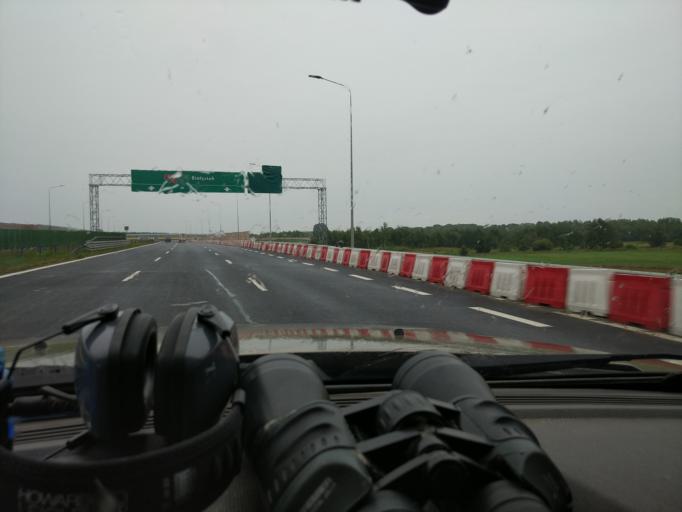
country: PL
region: Masovian Voivodeship
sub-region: Powiat wolominski
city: Kobylka
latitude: 52.3675
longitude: 21.1896
